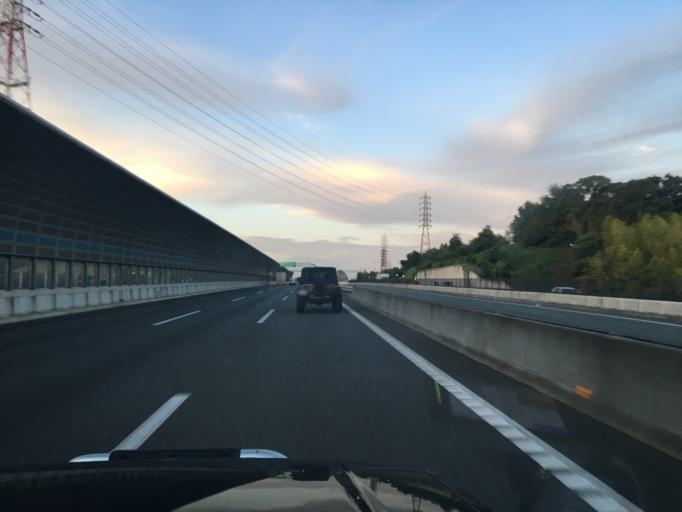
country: JP
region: Osaka
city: Neyagawa
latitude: 34.7614
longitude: 135.6493
